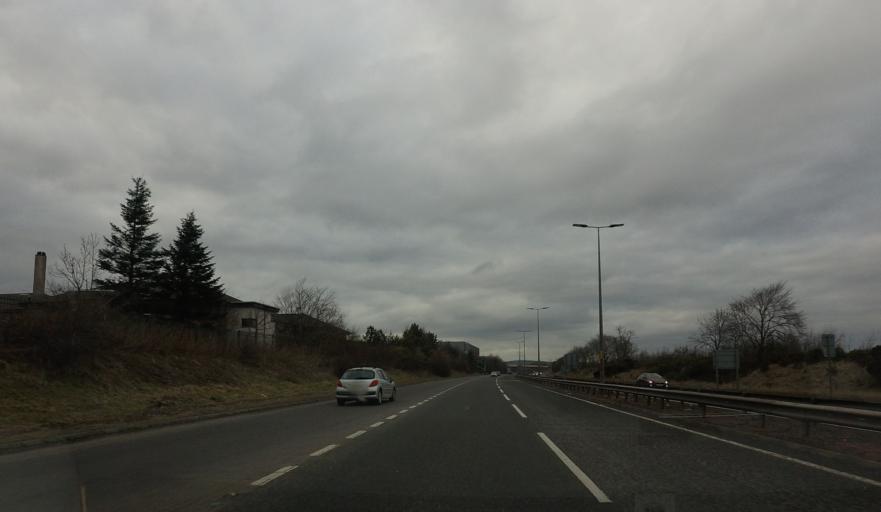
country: GB
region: Scotland
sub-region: Highland
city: Inverness
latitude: 57.4744
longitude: -4.1868
